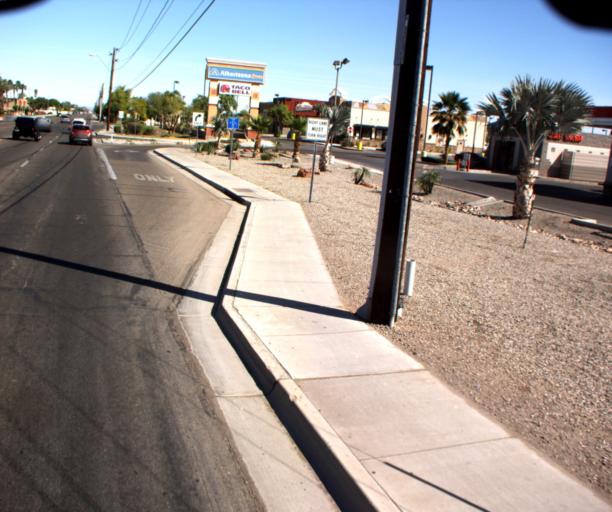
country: US
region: Arizona
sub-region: Yuma County
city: Yuma
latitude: 32.6842
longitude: -114.6503
